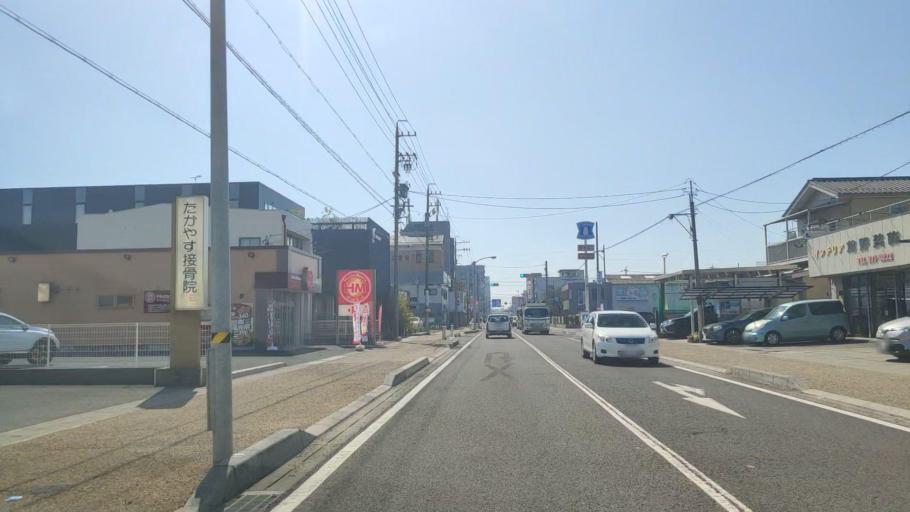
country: JP
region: Gifu
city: Gifu-shi
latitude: 35.4006
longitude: 136.7661
